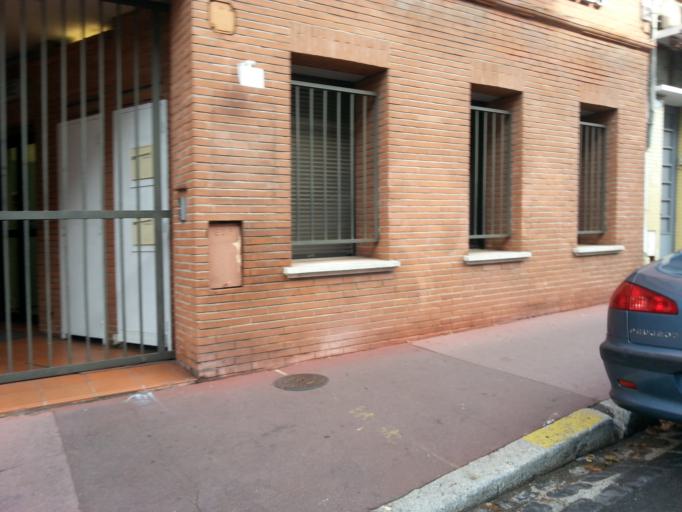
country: FR
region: Midi-Pyrenees
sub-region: Departement de la Haute-Garonne
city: Toulouse
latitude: 43.5959
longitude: 1.4634
